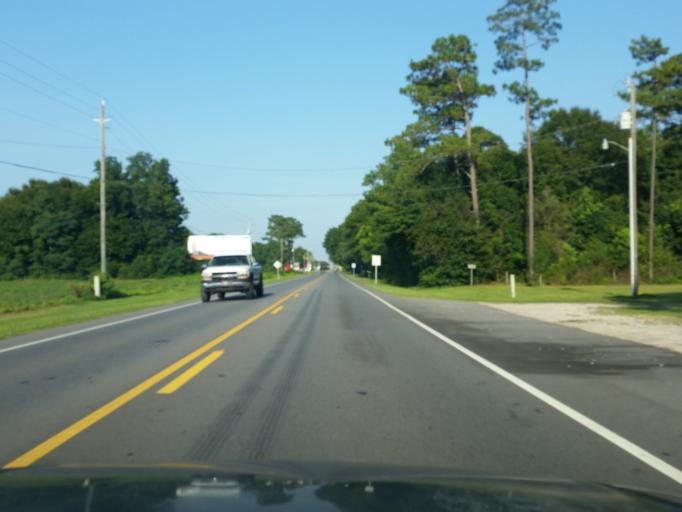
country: US
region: Alabama
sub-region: Baldwin County
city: Elberta
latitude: 30.4143
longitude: -87.6067
